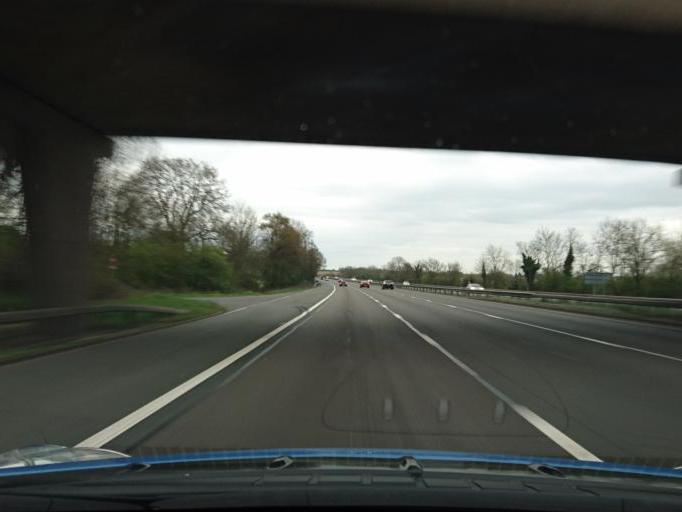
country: GB
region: England
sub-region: Staffordshire
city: Stone
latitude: 52.8975
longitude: -2.1845
